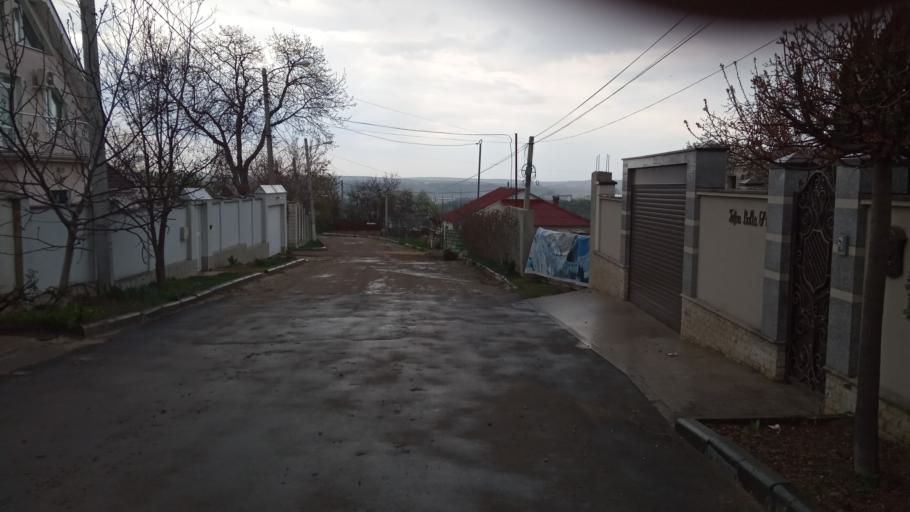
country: MD
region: Chisinau
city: Chisinau
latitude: 47.0102
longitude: 28.8106
